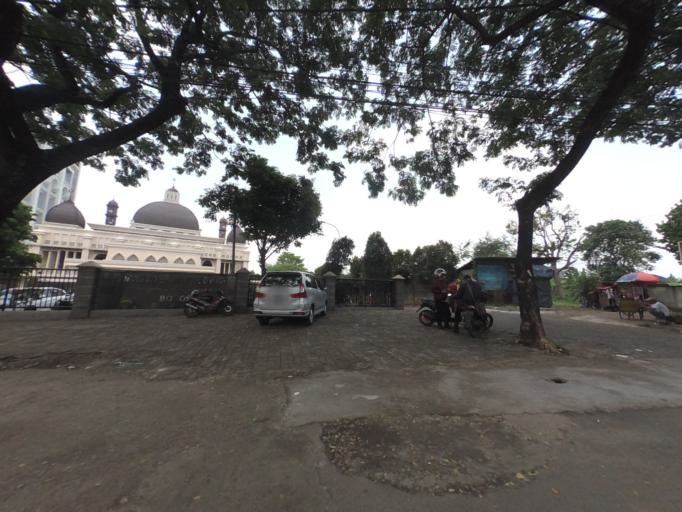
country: ID
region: West Java
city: Bogor
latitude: -6.5656
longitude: 106.7626
